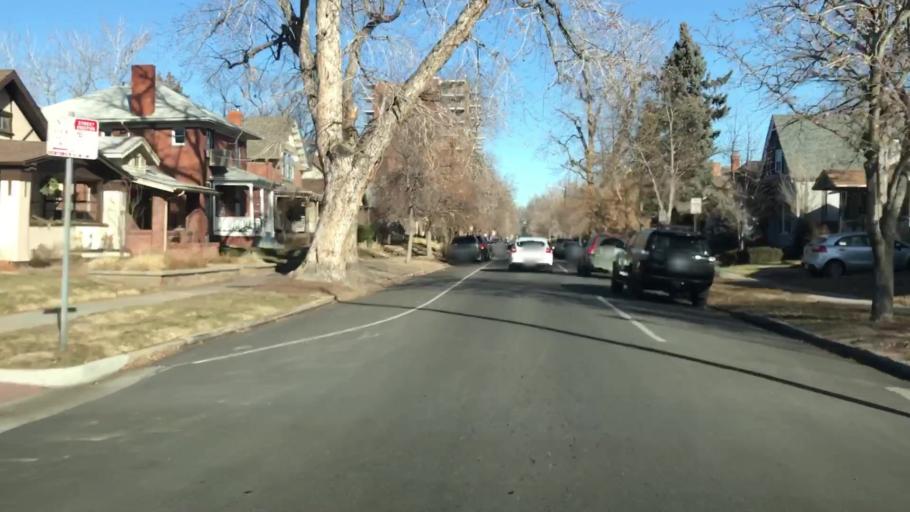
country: US
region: Colorado
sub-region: Denver County
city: Denver
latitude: 39.7225
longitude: -104.9776
